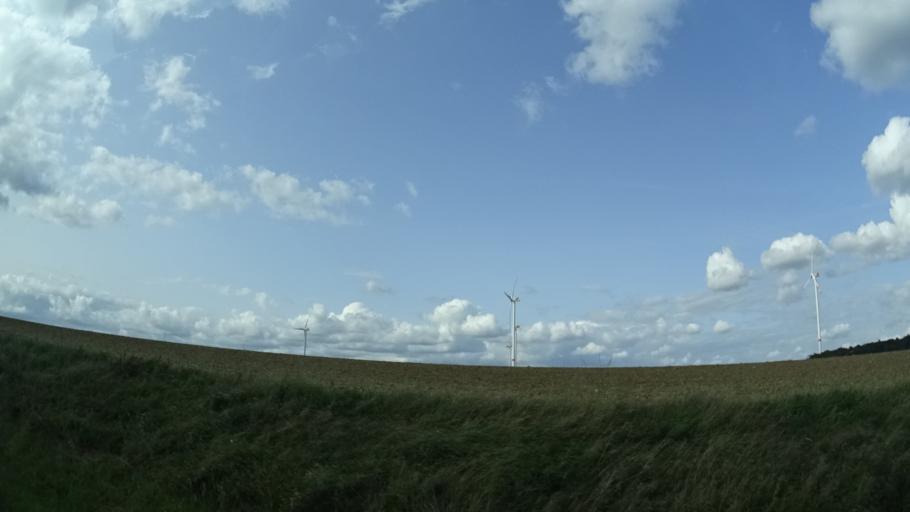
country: DE
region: Bavaria
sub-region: Regierungsbezirk Unterfranken
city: Retzstadt
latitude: 49.9154
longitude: 9.9059
